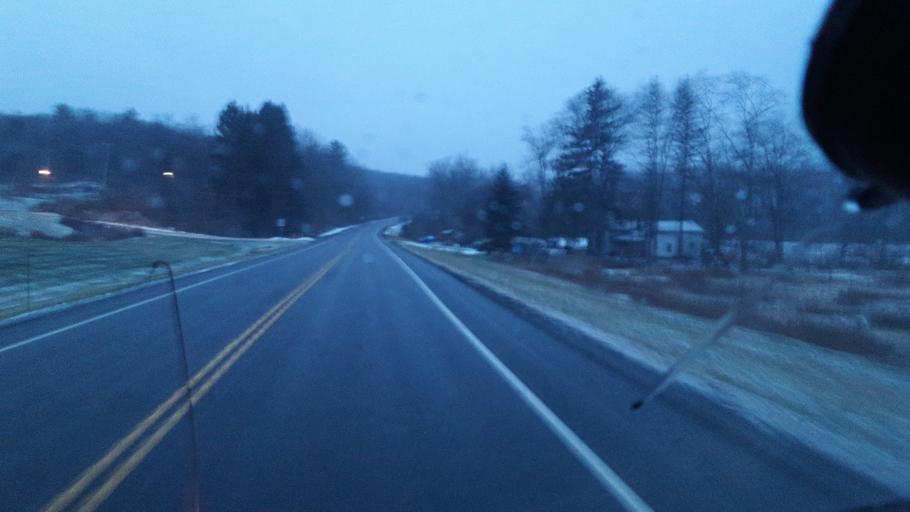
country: US
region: New York
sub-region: Allegany County
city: Belmont
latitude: 42.2632
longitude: -78.0649
